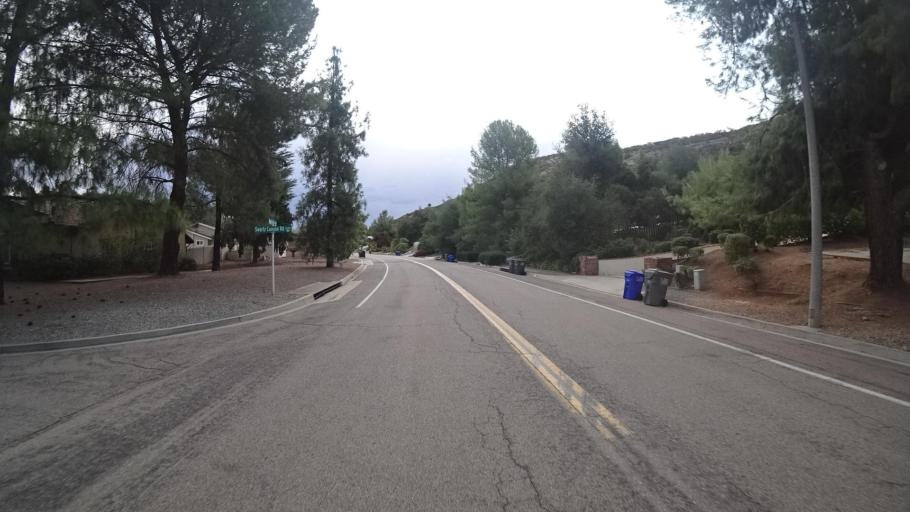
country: US
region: California
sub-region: San Diego County
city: San Diego Country Estates
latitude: 33.0097
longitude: -116.8078
